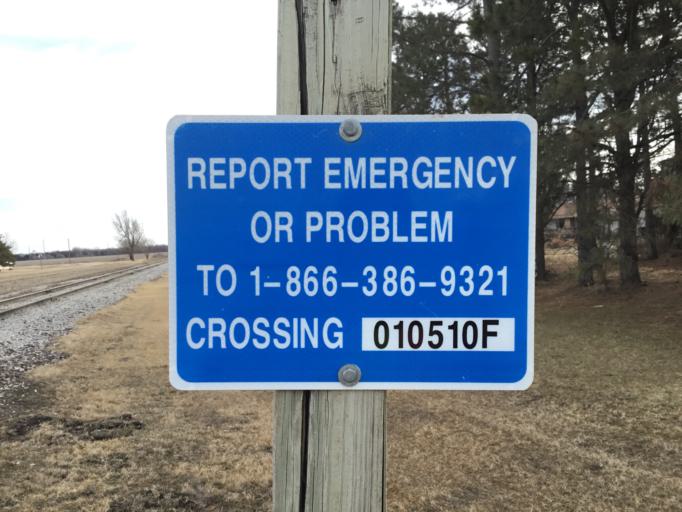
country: US
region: Kansas
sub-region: McPherson County
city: McPherson
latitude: 38.3704
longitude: -97.7036
